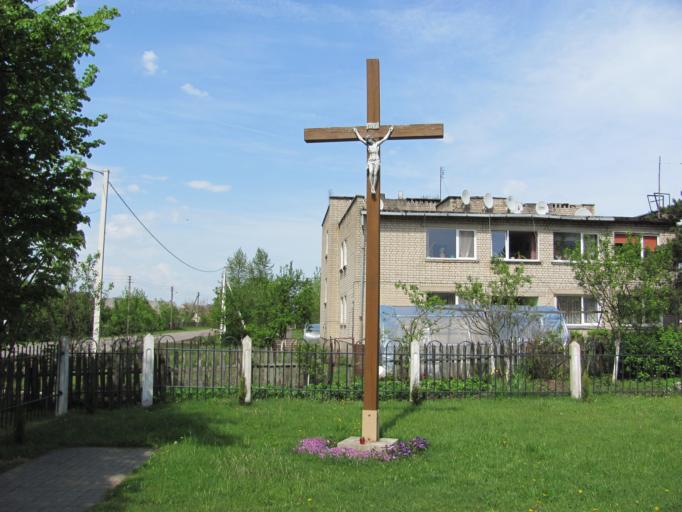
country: LT
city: Nemencine
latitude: 54.8047
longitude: 25.5161
